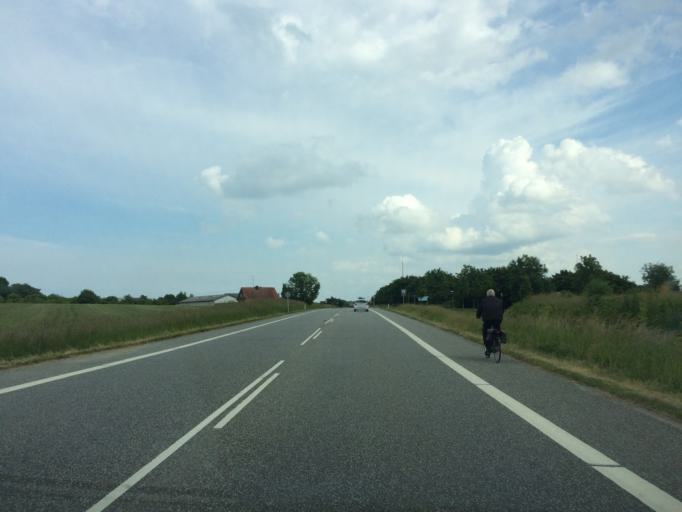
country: DK
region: South Denmark
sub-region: Fredericia Kommune
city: Snoghoj
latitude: 55.5331
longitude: 9.6997
